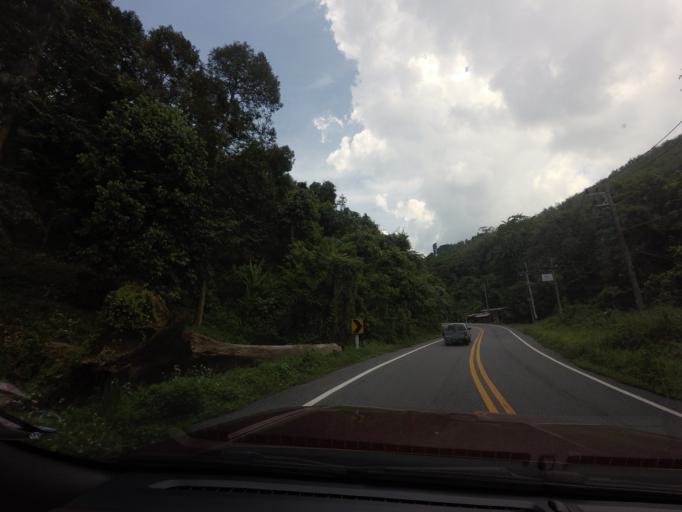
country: TH
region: Yala
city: Than To
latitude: 6.0347
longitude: 101.1975
